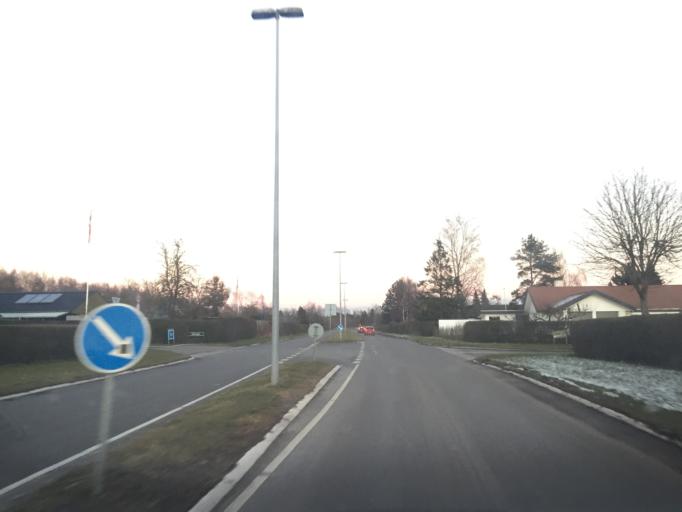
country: DK
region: Capital Region
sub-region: Hoje-Taastrup Kommune
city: Flong
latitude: 55.6499
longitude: 12.2212
